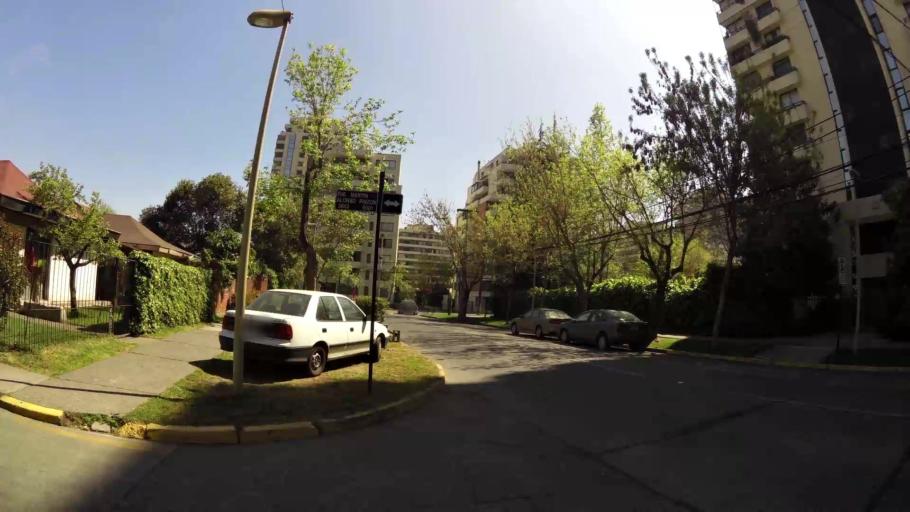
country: CL
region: Santiago Metropolitan
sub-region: Provincia de Santiago
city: Villa Presidente Frei, Nunoa, Santiago, Chile
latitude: -33.4192
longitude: -70.5608
